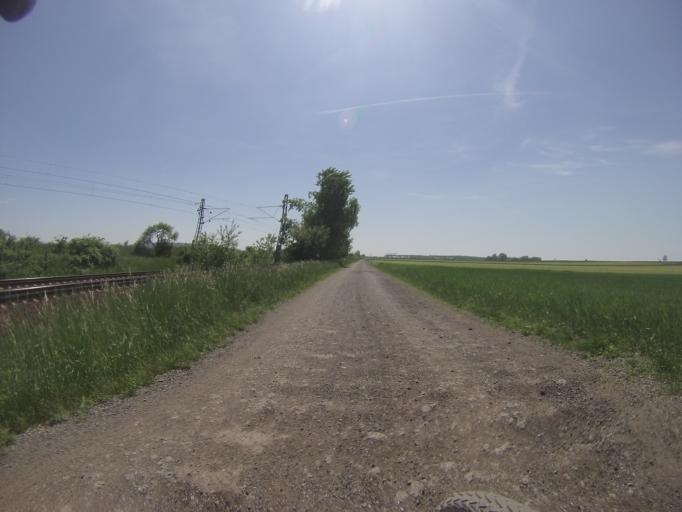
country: CZ
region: South Moravian
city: Vranovice
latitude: 48.9849
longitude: 16.5986
